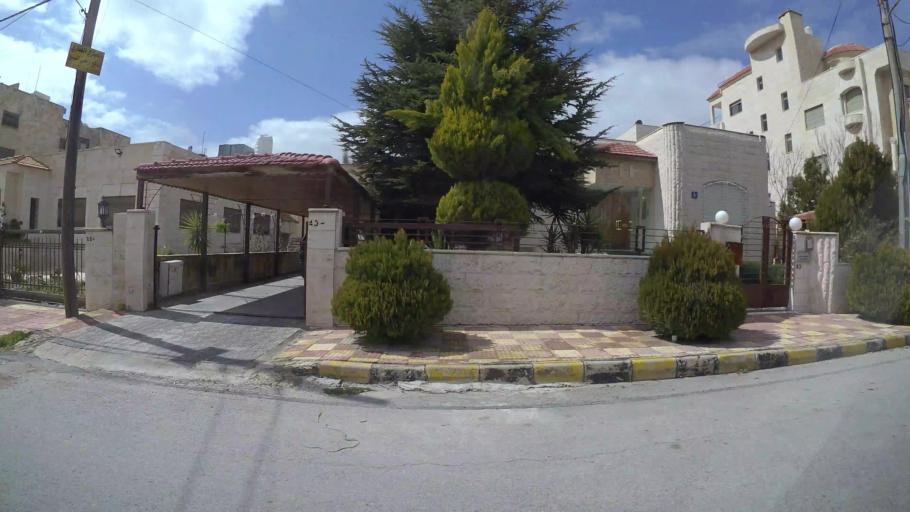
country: JO
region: Amman
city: Al Jubayhah
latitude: 31.9943
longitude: 35.8463
